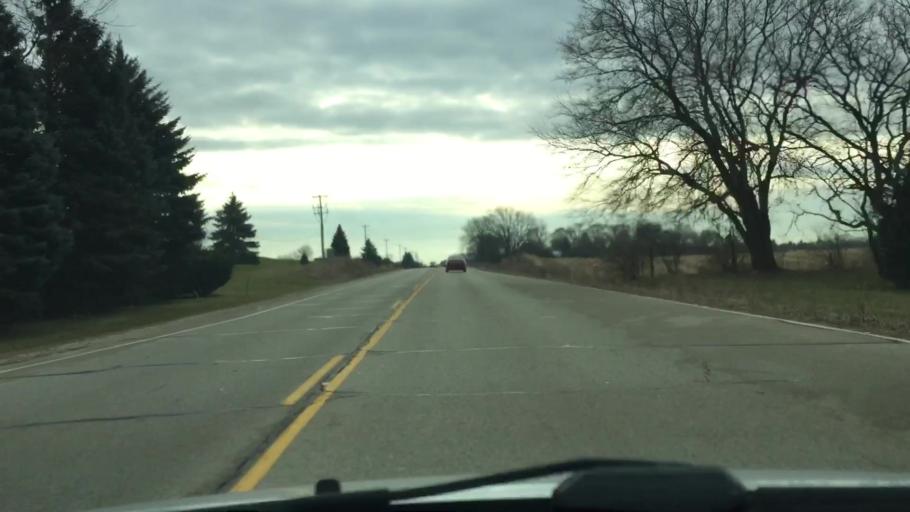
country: US
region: Wisconsin
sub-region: Walworth County
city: Elkhorn
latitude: 42.7536
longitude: -88.5537
